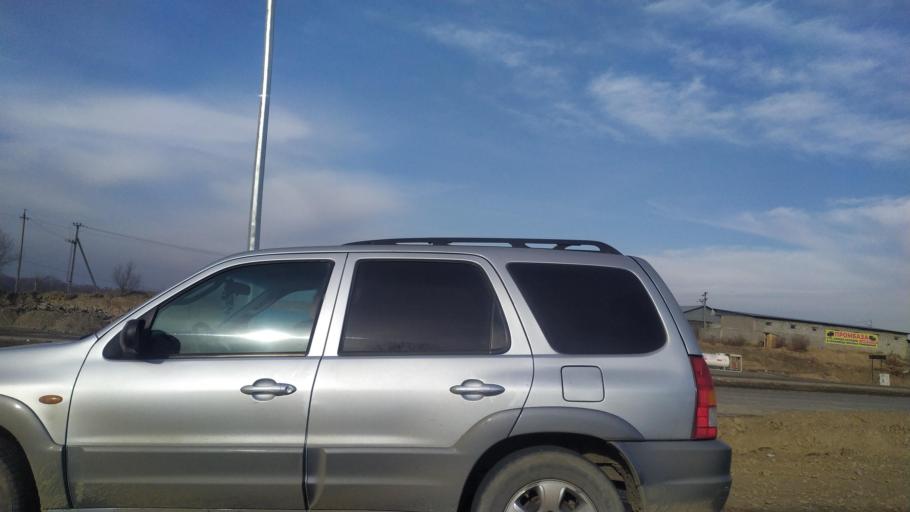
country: KZ
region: Almaty Oblysy
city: Burunday
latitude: 43.2235
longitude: 76.7231
